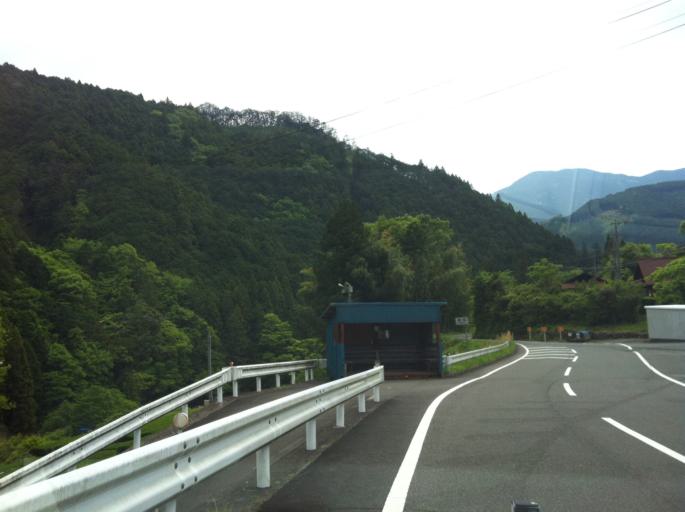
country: JP
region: Shizuoka
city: Shizuoka-shi
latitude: 35.1270
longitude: 138.2999
